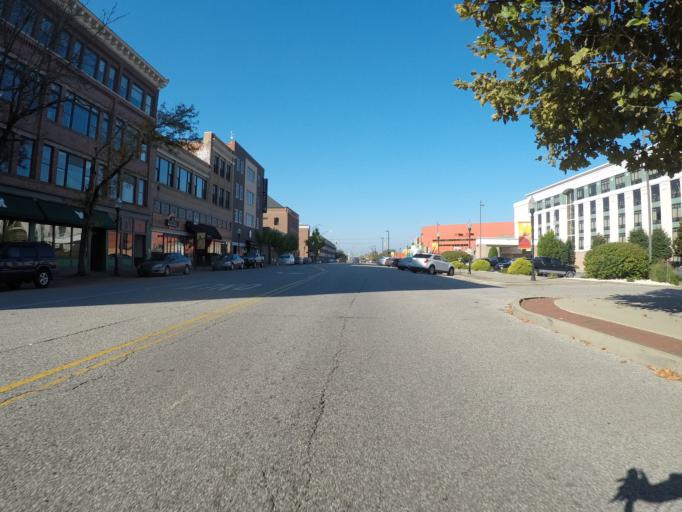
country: US
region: West Virginia
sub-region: Cabell County
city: Huntington
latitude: 38.4219
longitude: -82.4444
